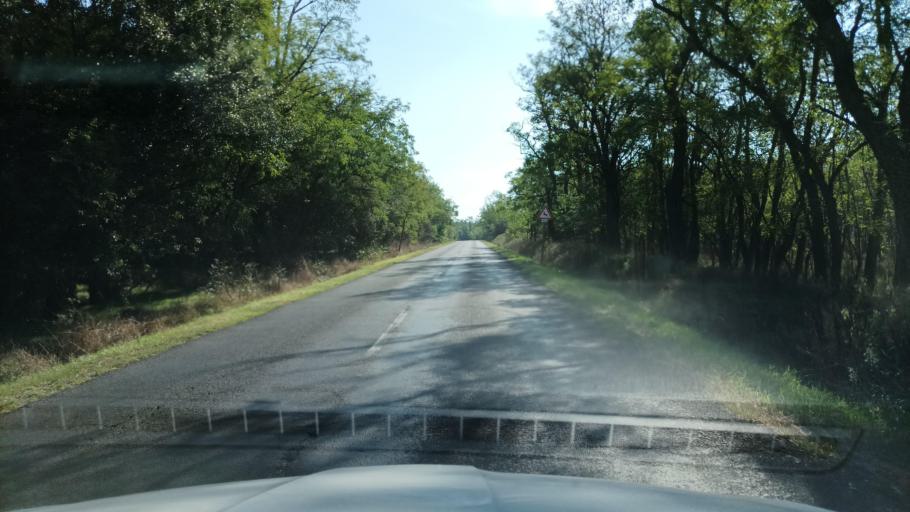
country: HU
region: Pest
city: Isaszeg
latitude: 47.5775
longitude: 19.4085
